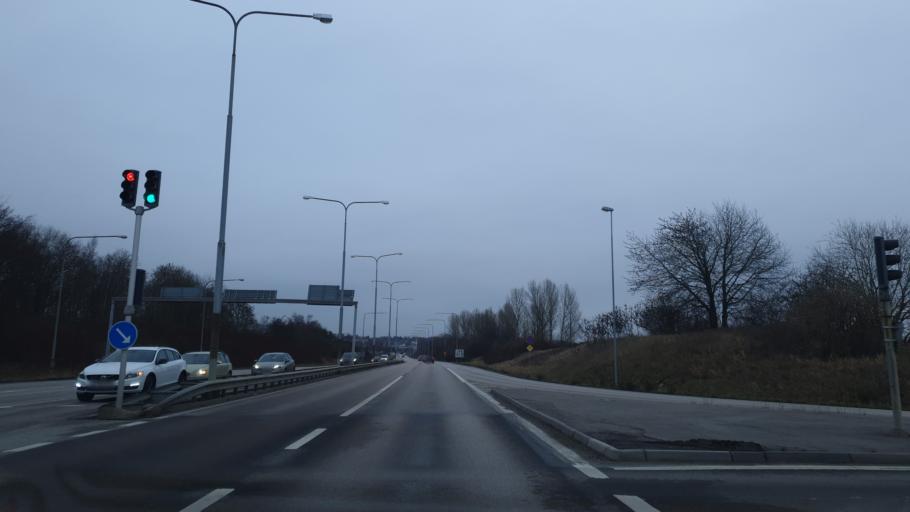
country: SE
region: Blekinge
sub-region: Karlskrona Kommun
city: Karlskrona
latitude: 56.1964
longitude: 15.6321
